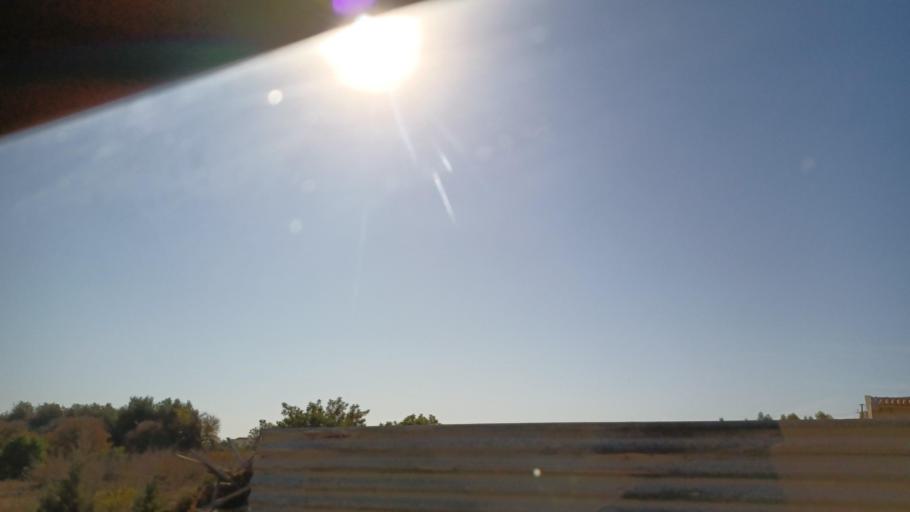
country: CY
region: Larnaka
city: Kolossi
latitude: 34.6717
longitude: 32.9495
